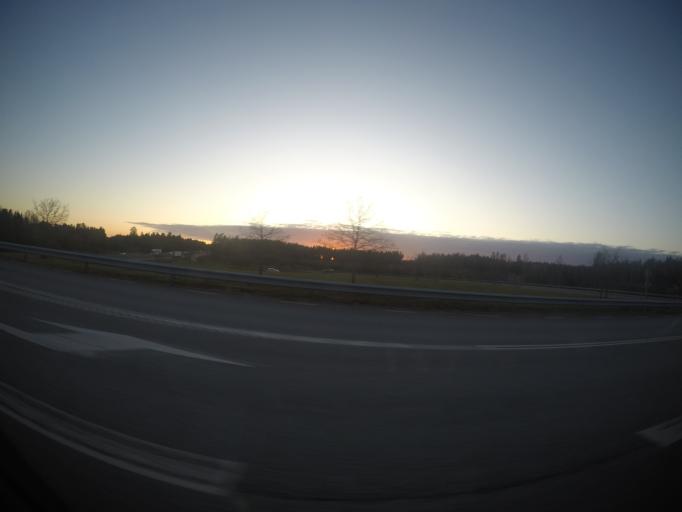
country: SE
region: OErebro
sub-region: Orebro Kommun
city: Orebro
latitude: 59.3038
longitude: 15.2585
